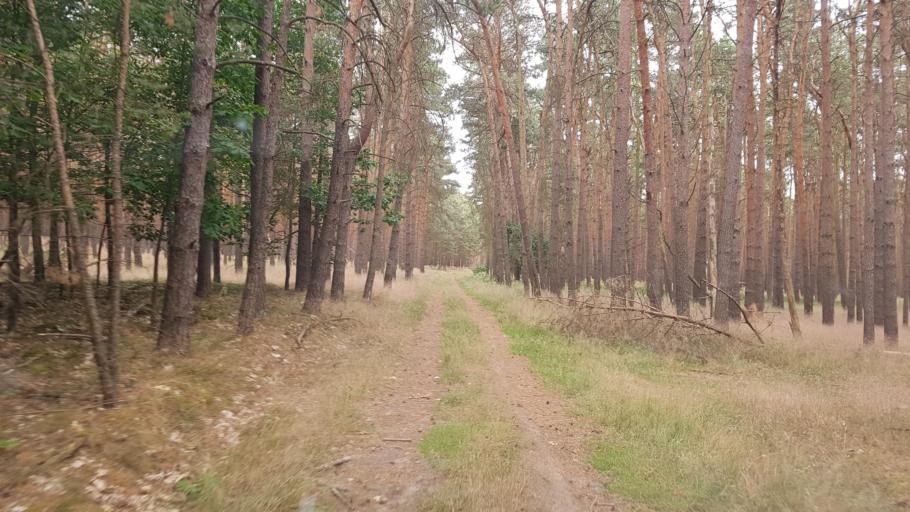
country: DE
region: Brandenburg
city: Treuenbrietzen
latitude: 52.0358
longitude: 12.8401
